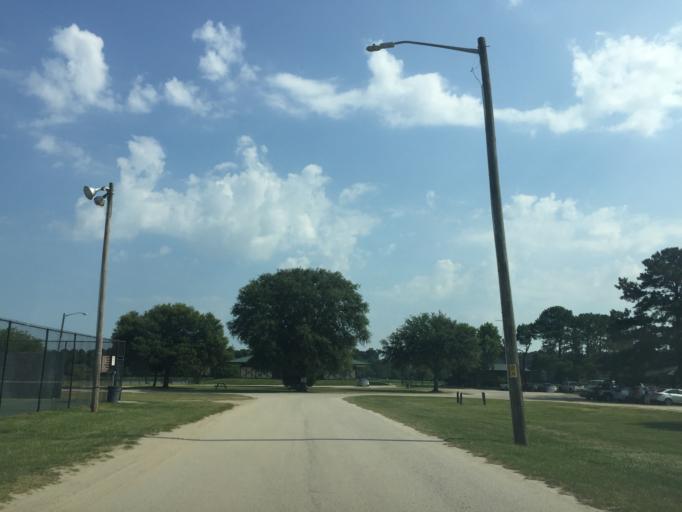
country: US
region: Georgia
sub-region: Chatham County
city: Isle of Hope
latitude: 31.9918
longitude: -81.0879
